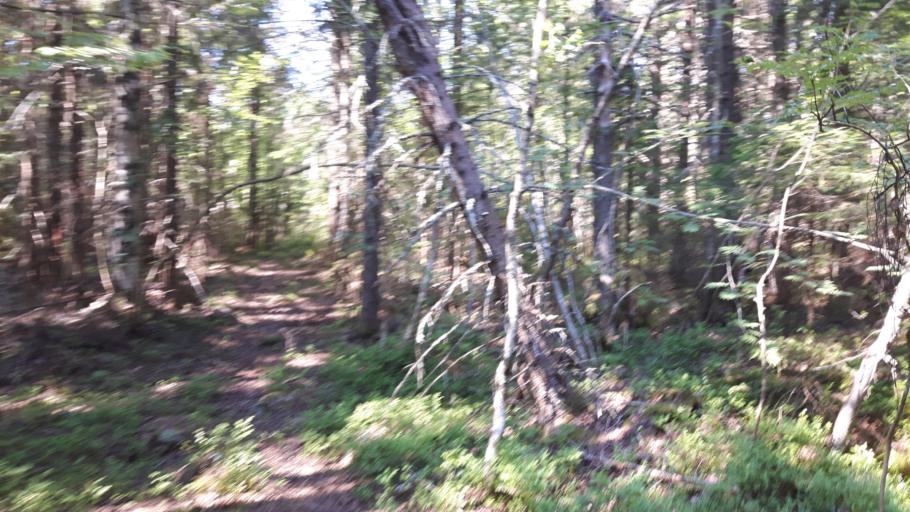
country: SE
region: Vaesternorrland
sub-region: Timra Kommun
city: Soraker
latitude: 62.6508
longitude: 17.5163
